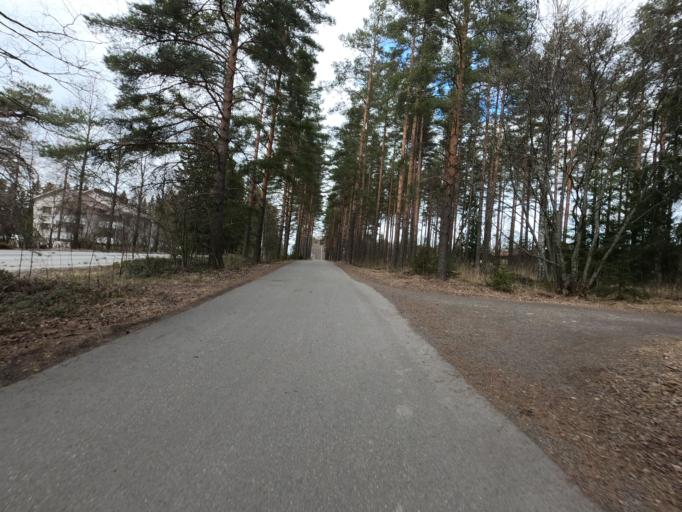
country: FI
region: North Karelia
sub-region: Joensuu
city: Joensuu
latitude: 62.5770
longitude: 29.8009
